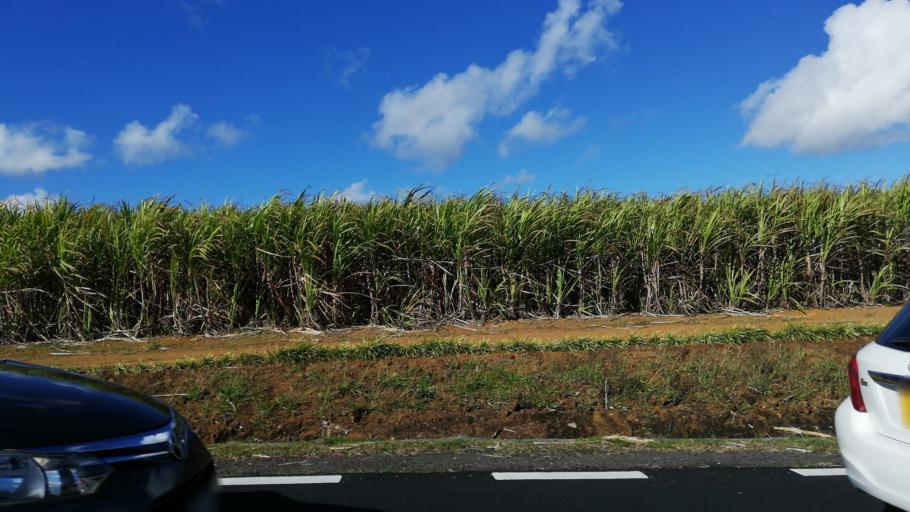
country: MU
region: Moka
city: La Dagotiere
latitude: -20.2334
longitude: 57.5648
